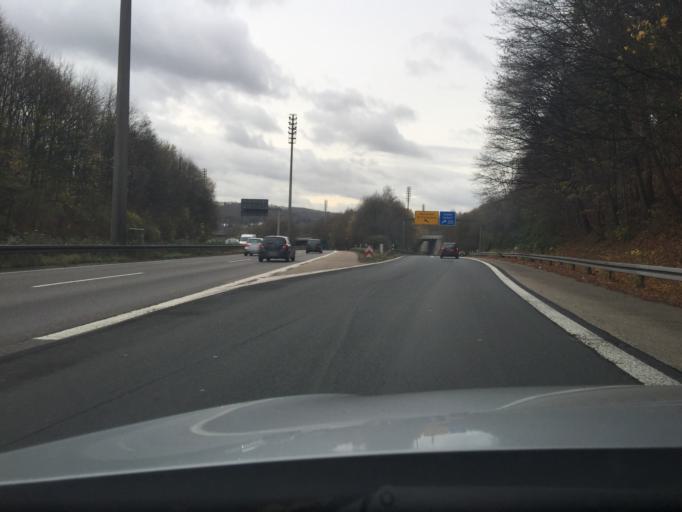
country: DE
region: North Rhine-Westphalia
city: Wulfrath
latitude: 51.2460
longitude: 7.0961
